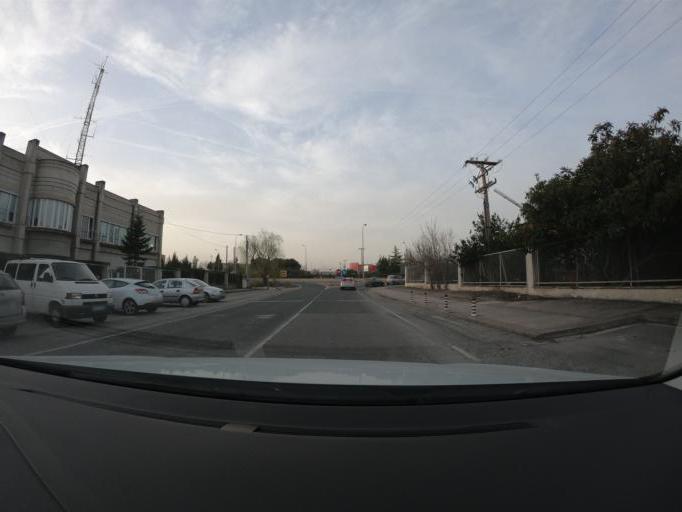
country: ES
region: La Rioja
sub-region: Provincia de La Rioja
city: Logrono
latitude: 42.4553
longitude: -2.4717
